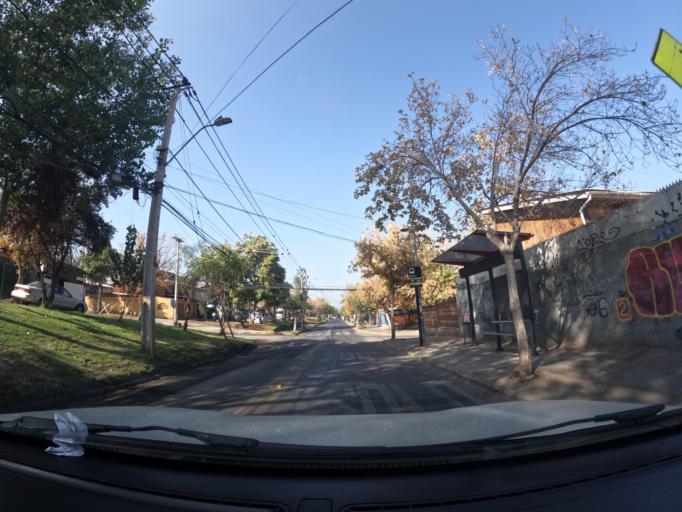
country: CL
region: Santiago Metropolitan
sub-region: Provincia de Santiago
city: Villa Presidente Frei, Nunoa, Santiago, Chile
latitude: -33.4746
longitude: -70.5368
